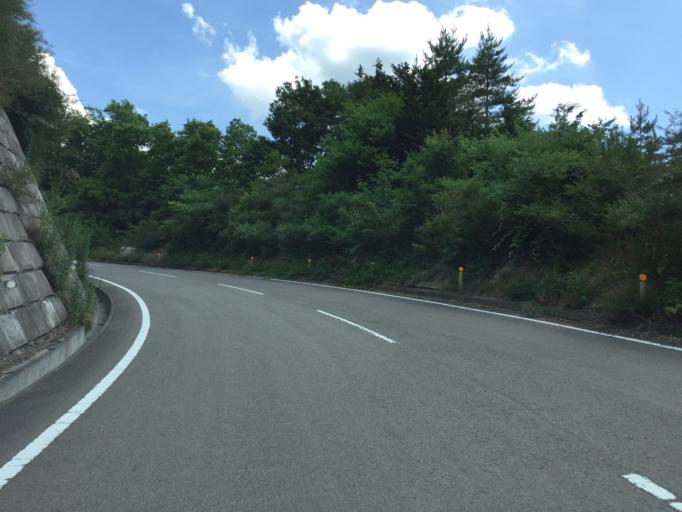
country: JP
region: Fukushima
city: Yanagawamachi-saiwaicho
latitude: 37.7697
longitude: 140.6730
